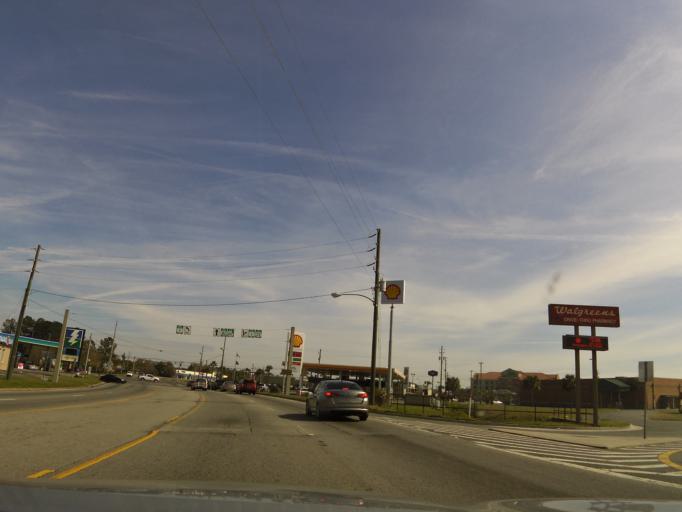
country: US
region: Georgia
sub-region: Ware County
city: Waycross
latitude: 31.2061
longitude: -82.3385
